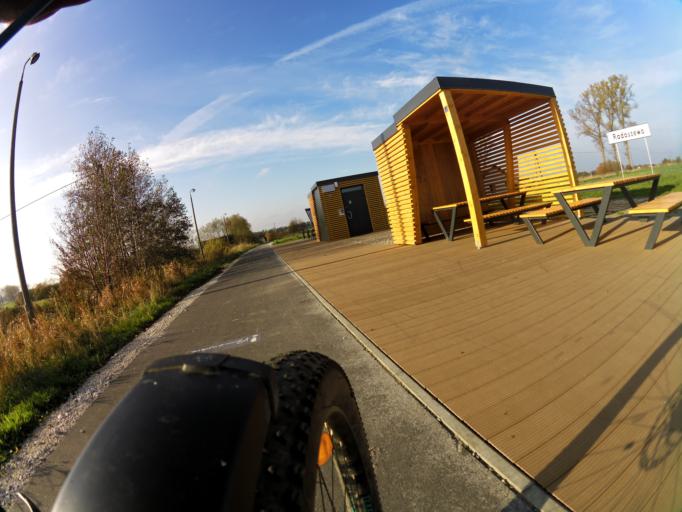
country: PL
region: Pomeranian Voivodeship
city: Strzelno
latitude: 54.7651
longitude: 18.2726
